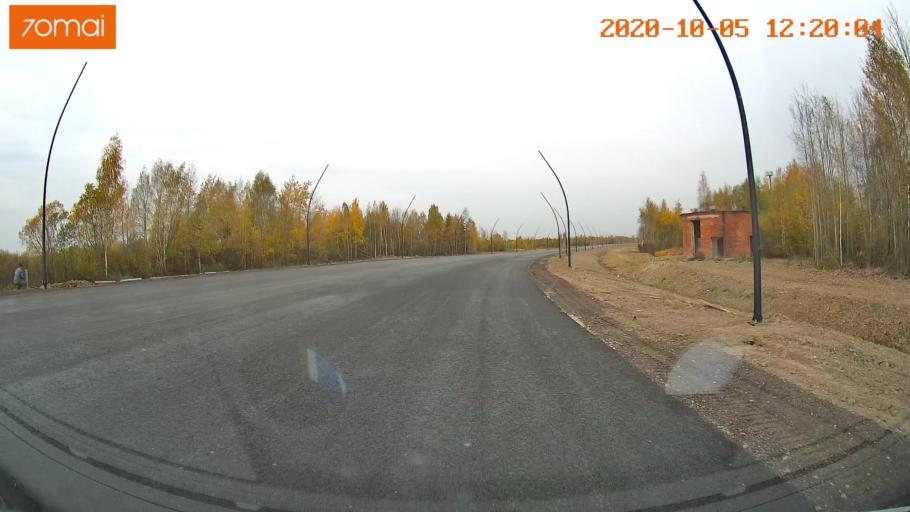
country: RU
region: Ivanovo
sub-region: Gorod Ivanovo
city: Ivanovo
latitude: 56.9595
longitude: 40.9314
